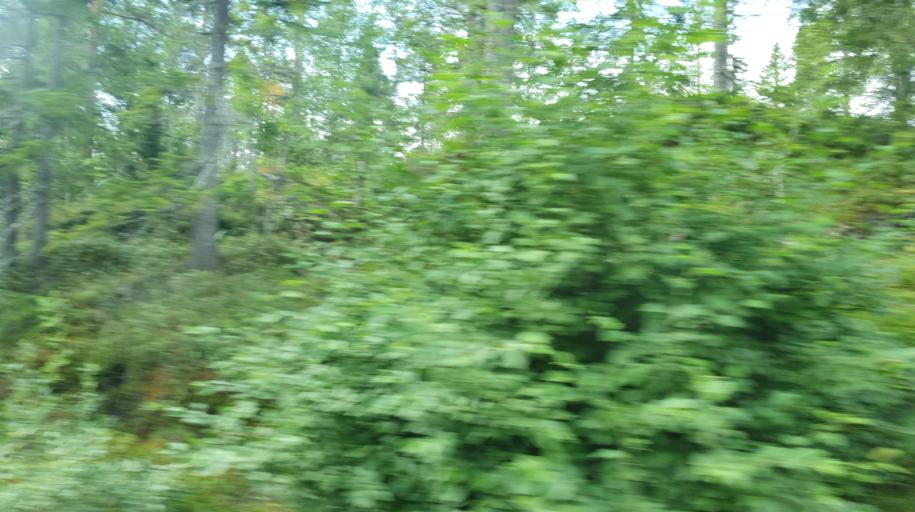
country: NO
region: Nord-Trondelag
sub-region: Levanger
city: Skogn
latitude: 63.5856
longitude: 11.2439
